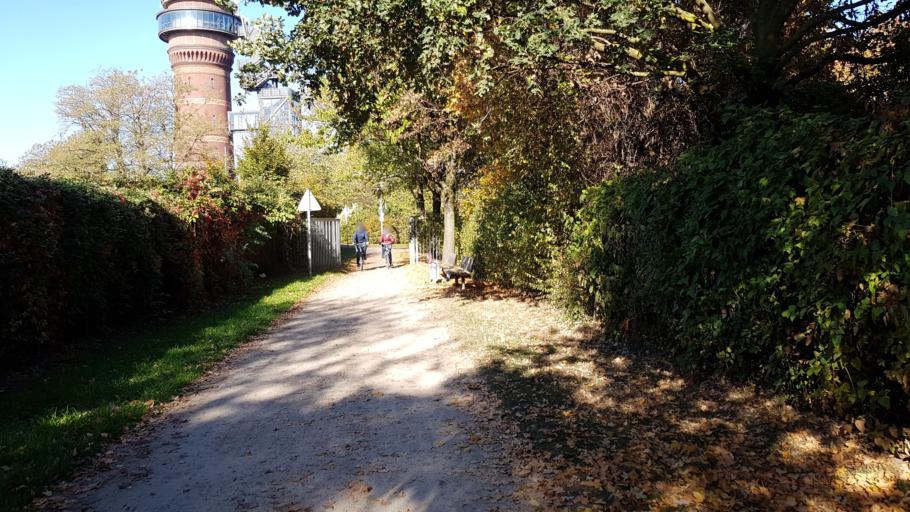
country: DE
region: North Rhine-Westphalia
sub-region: Regierungsbezirk Dusseldorf
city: Muelheim (Ruhr)
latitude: 51.4423
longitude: 6.8582
